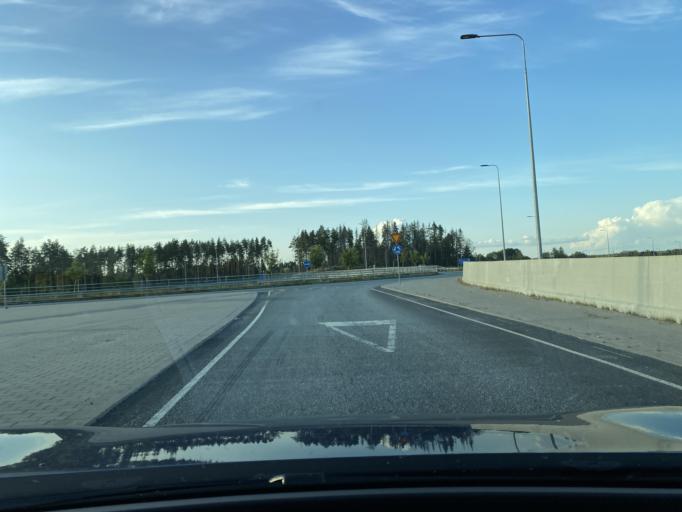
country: FI
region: Southern Ostrobothnia
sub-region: Seinaejoki
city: Nurmo
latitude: 62.8208
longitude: 22.9141
